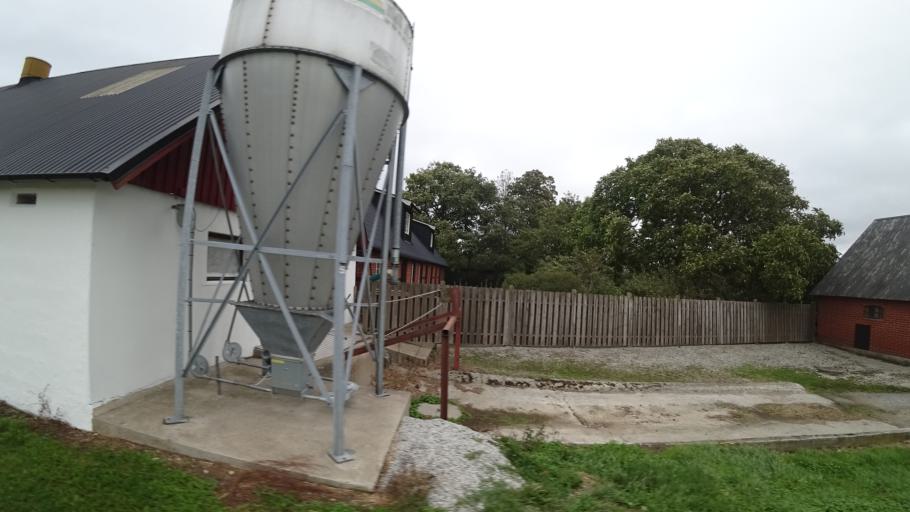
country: SE
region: Skane
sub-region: Kavlinge Kommun
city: Kaevlinge
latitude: 55.7728
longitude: 13.1119
